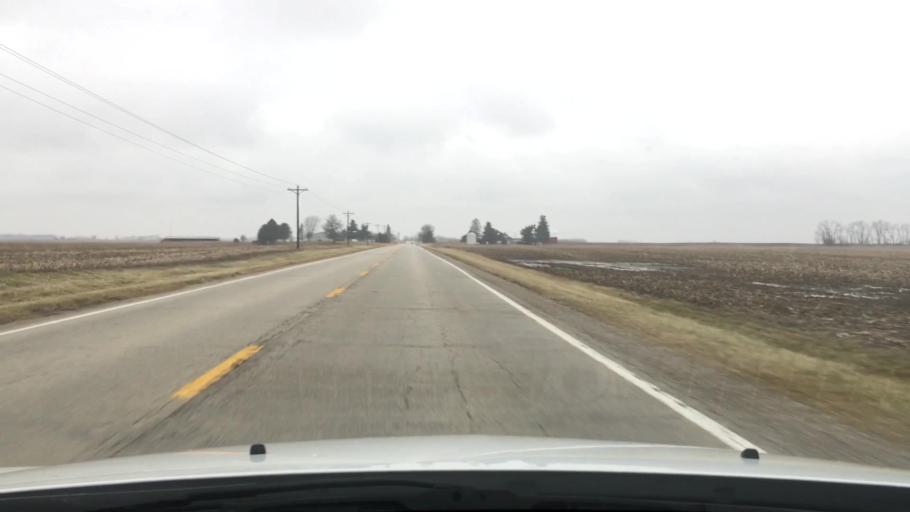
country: US
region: Illinois
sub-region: Iroquois County
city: Watseka
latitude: 40.8904
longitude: -87.6993
